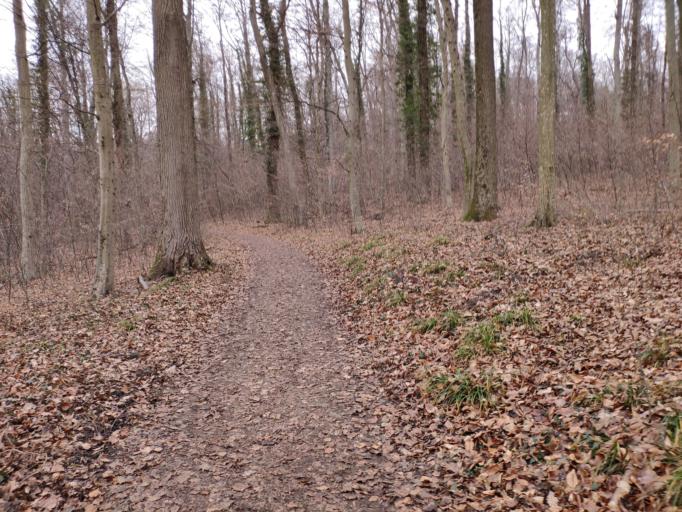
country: CH
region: Basel-City
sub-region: Basel-Stadt
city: Bettingen
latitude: 47.5595
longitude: 7.6494
